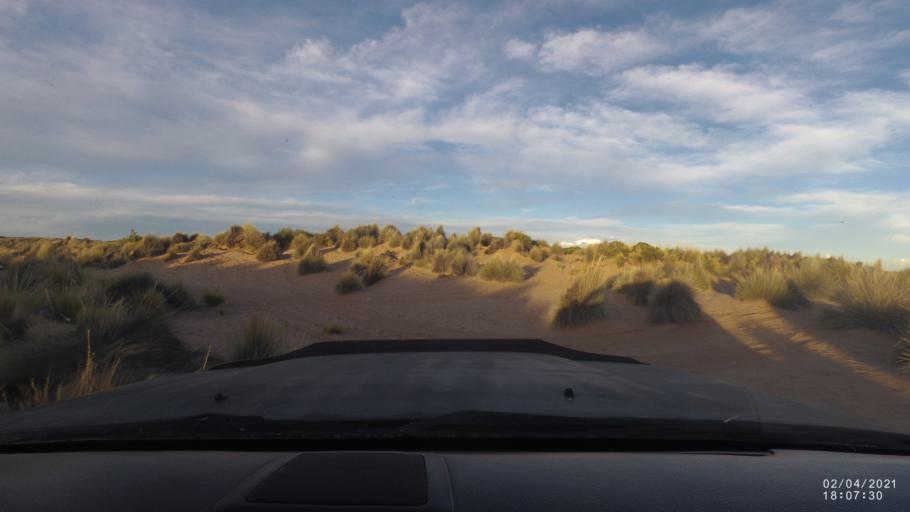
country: BO
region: Oruro
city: Poopo
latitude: -18.7095
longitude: -67.5391
